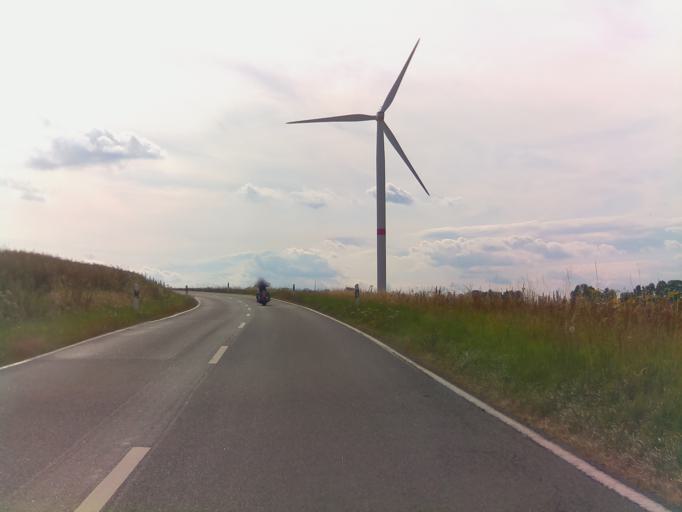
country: DE
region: Baden-Wuerttemberg
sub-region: Regierungsbezirk Stuttgart
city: Buch am Ahorn
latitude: 49.5320
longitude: 9.4872
